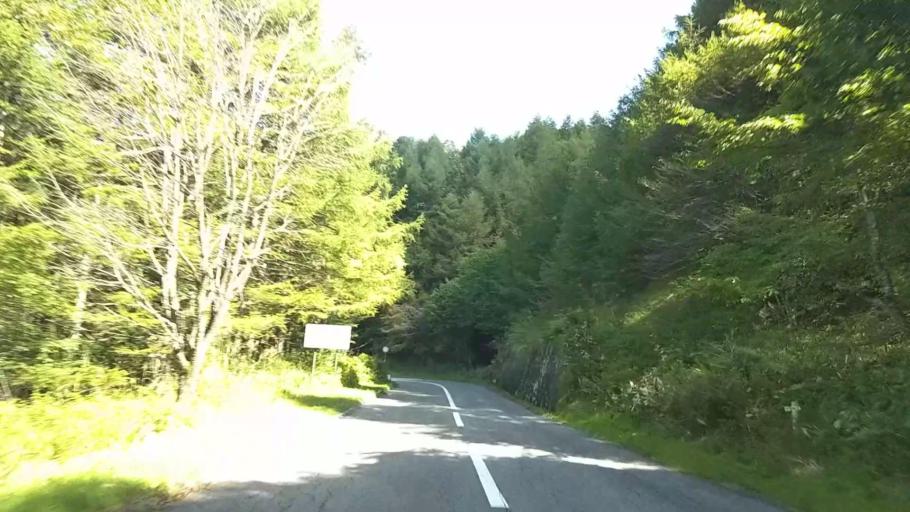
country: JP
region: Nagano
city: Suwa
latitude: 36.1918
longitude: 138.1245
